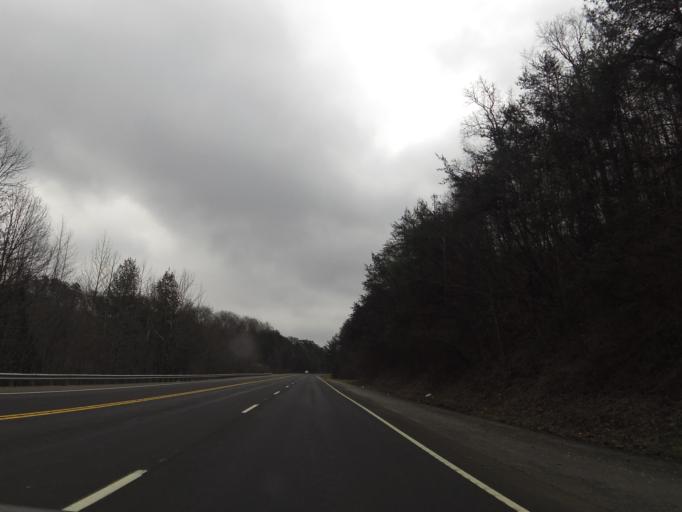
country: US
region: Tennessee
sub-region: Scott County
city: Huntsville
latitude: 36.4019
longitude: -84.4459
